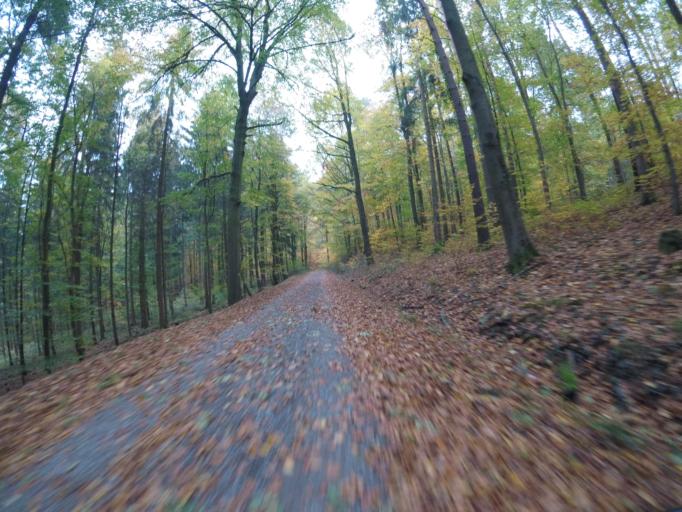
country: DE
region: Baden-Wuerttemberg
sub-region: Regierungsbezirk Stuttgart
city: Grossbottwar
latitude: 49.0006
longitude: 9.3149
